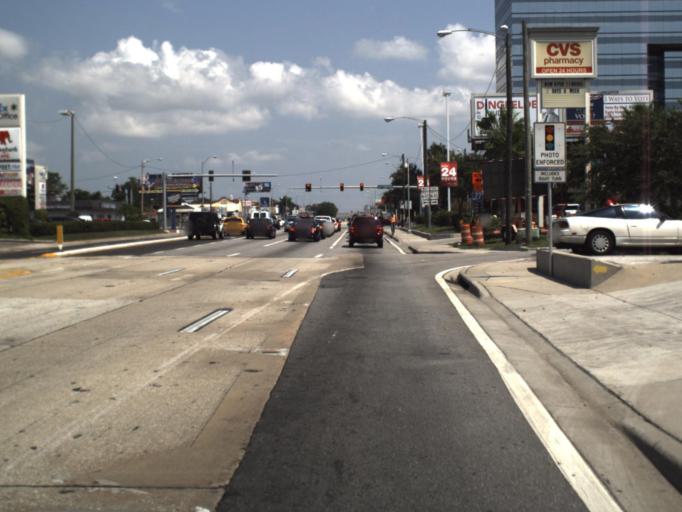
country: US
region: Florida
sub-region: Hillsborough County
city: Tampa
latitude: 27.9436
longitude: -82.5056
